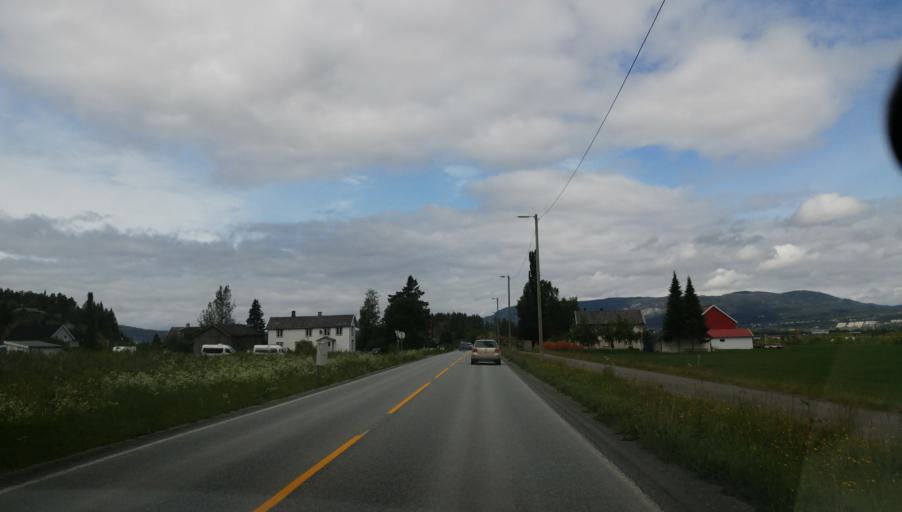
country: NO
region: Nord-Trondelag
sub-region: Stjordal
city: Stjordalshalsen
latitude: 63.4383
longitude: 10.9268
